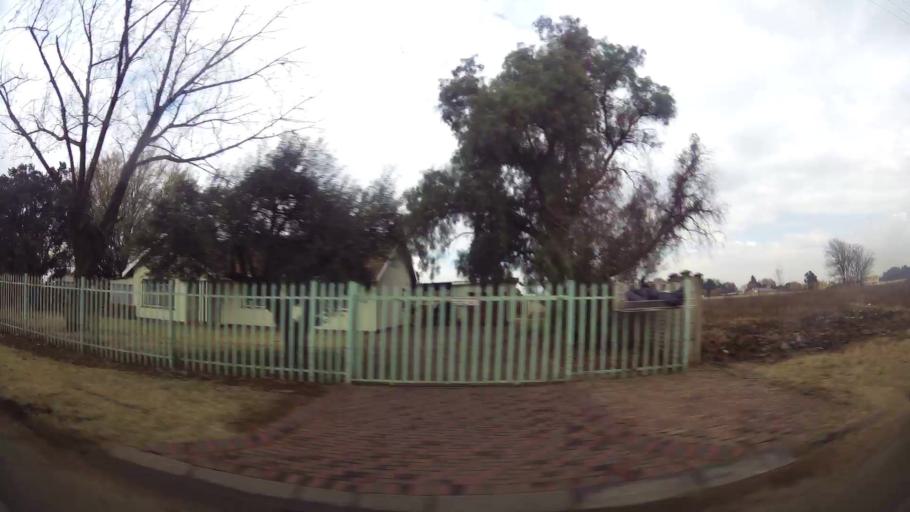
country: ZA
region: Gauteng
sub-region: Sedibeng District Municipality
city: Meyerton
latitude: -26.5848
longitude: 28.0014
